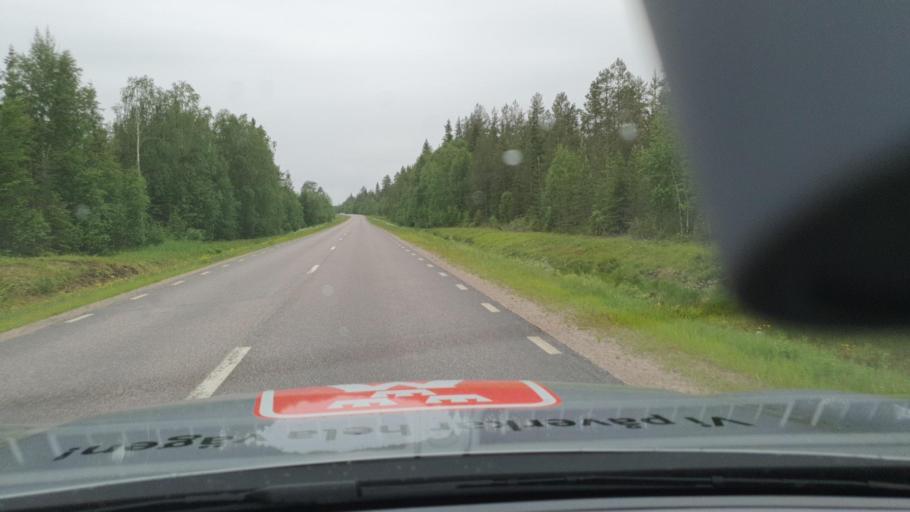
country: SE
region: Norrbotten
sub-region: Overtornea Kommun
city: OEvertornea
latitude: 66.4004
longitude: 23.4999
